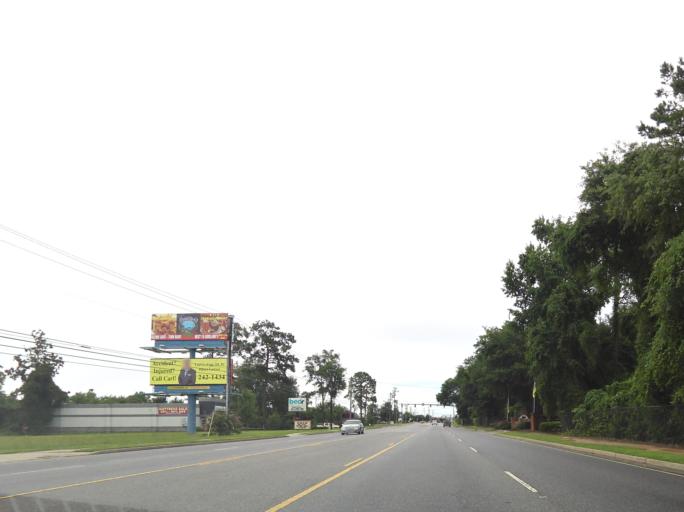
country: US
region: Georgia
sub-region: Lowndes County
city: Remerton
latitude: 30.8359
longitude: -83.3209
